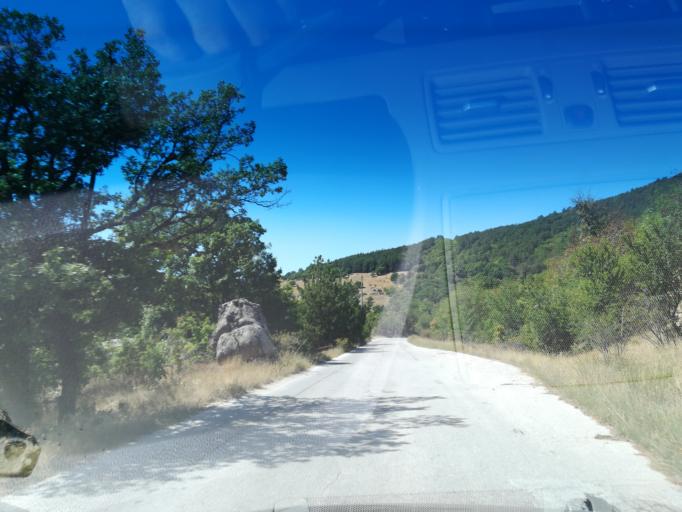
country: BG
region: Pazardzhik
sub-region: Obshtina Strelcha
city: Strelcha
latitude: 42.5472
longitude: 24.3329
